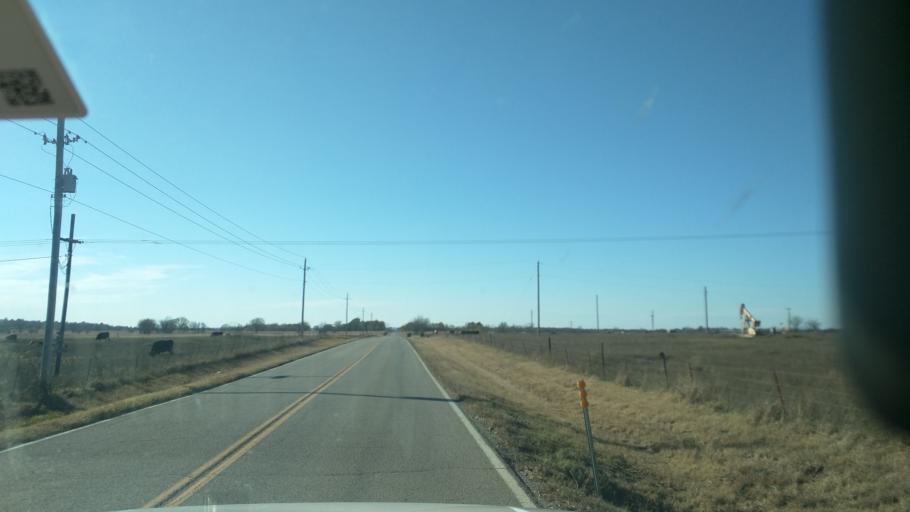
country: US
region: Oklahoma
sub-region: Nowata County
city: Nowata
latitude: 36.7716
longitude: -95.5425
